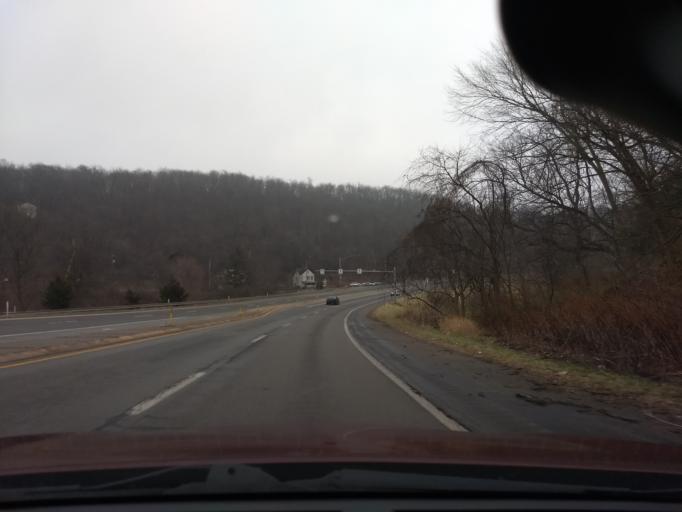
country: US
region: Pennsylvania
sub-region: Allegheny County
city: East Pittsburgh
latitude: 40.3957
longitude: -79.8292
